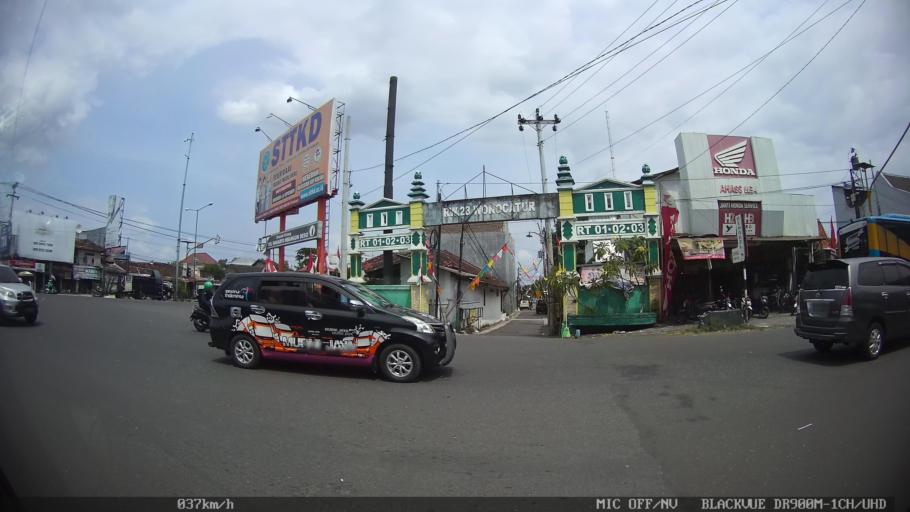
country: ID
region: Daerah Istimewa Yogyakarta
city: Depok
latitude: -7.7985
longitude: 110.4095
